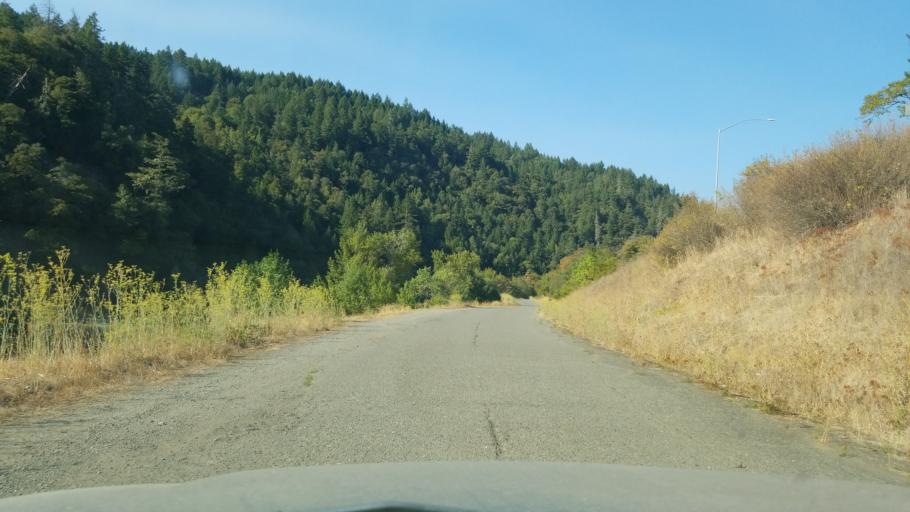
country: US
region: California
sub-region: Humboldt County
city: Redway
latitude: 40.1765
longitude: -123.7816
